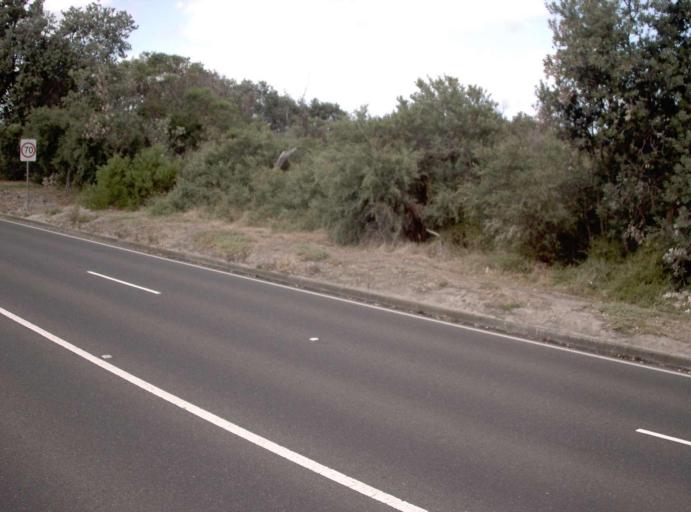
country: AU
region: Victoria
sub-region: Frankston
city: Seaford
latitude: -38.1076
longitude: 145.1258
